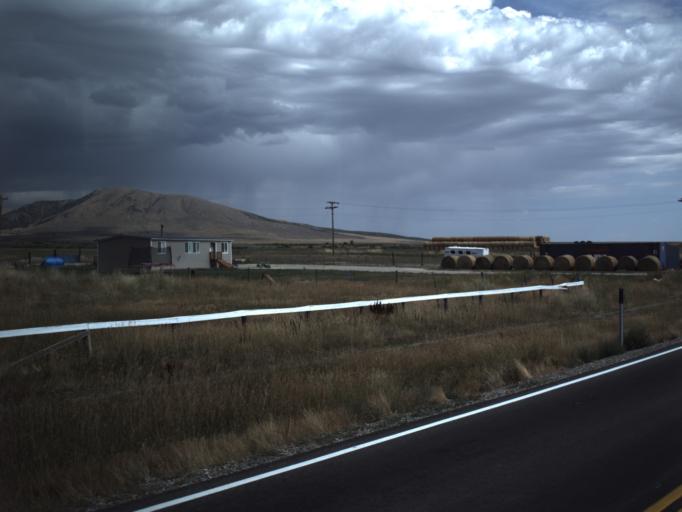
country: US
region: Idaho
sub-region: Cassia County
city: Burley
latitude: 41.8170
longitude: -113.3282
